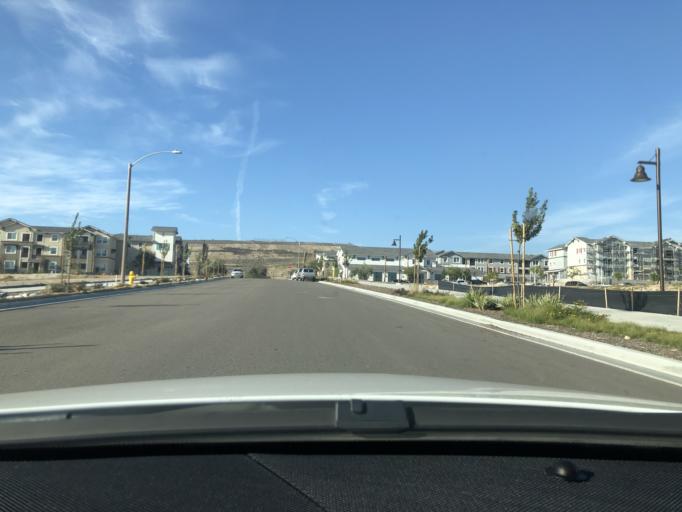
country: US
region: California
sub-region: San Diego County
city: Bonita
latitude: 32.5982
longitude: -116.9989
